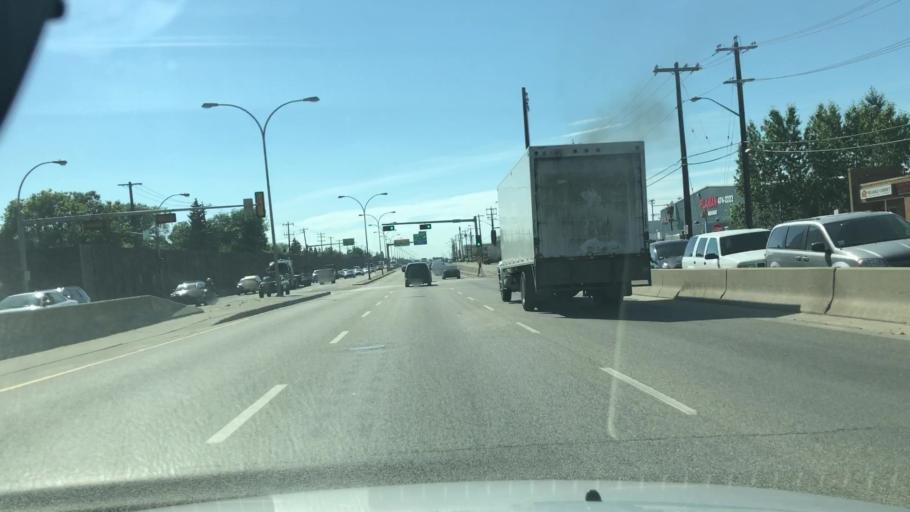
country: CA
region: Alberta
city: Edmonton
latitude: 53.5816
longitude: -113.4769
